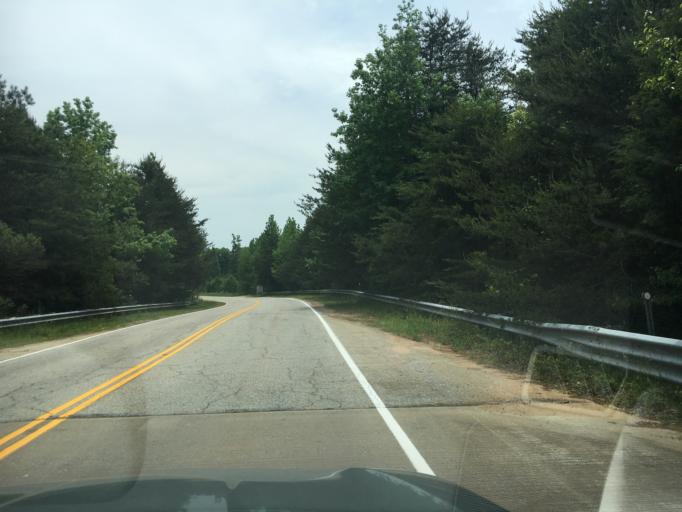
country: US
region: South Carolina
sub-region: Spartanburg County
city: Fairforest
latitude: 34.9766
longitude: -82.0159
